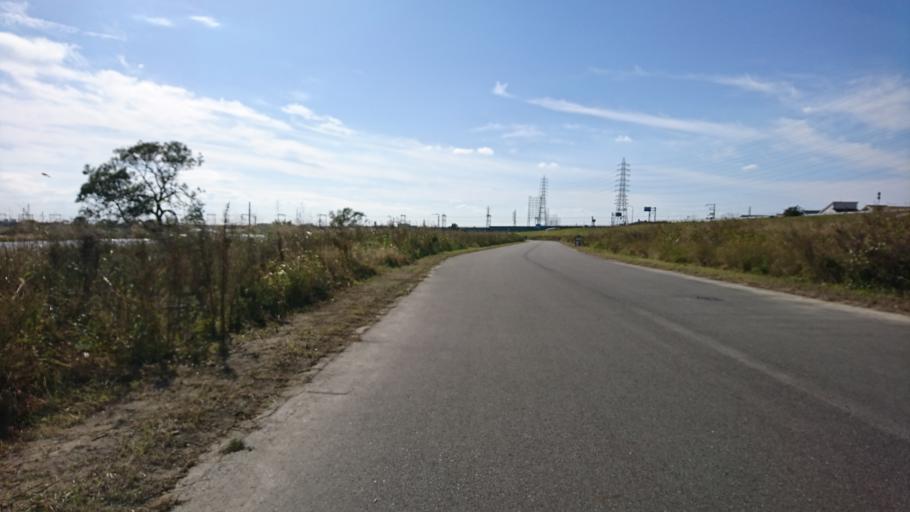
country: JP
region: Hyogo
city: Kakogawacho-honmachi
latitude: 34.7660
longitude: 134.8081
